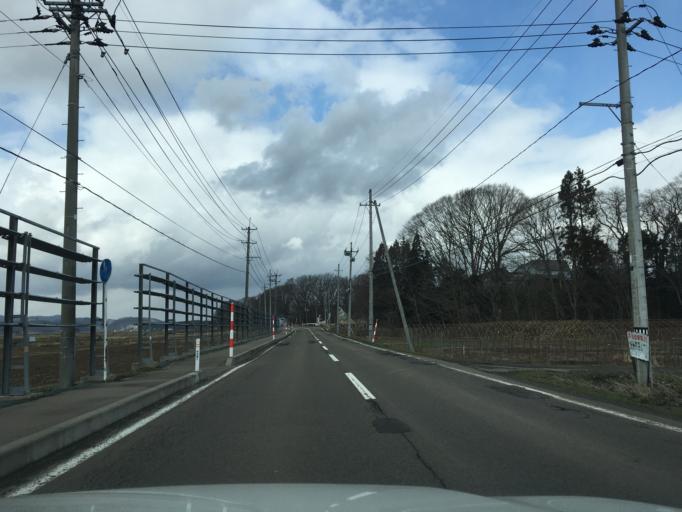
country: JP
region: Akita
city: Takanosu
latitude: 40.1419
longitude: 140.3490
